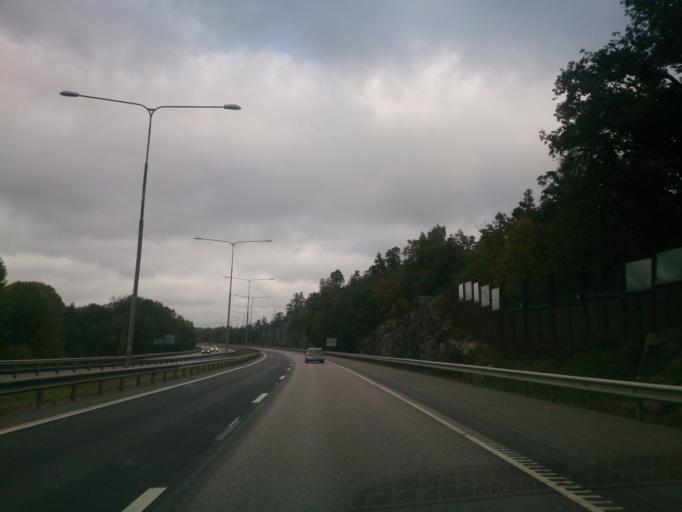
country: SE
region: Stockholm
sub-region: Nacka Kommun
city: Alta
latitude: 59.2370
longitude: 18.1228
